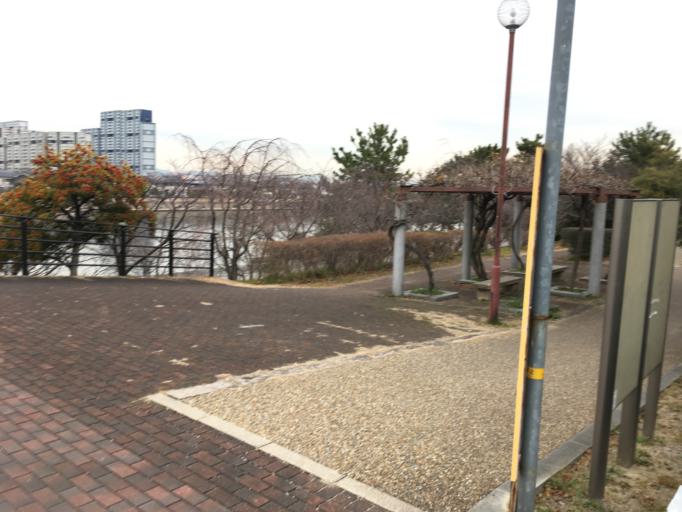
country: JP
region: Hyogo
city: Nishinomiya-hama
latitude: 34.7149
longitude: 135.3165
